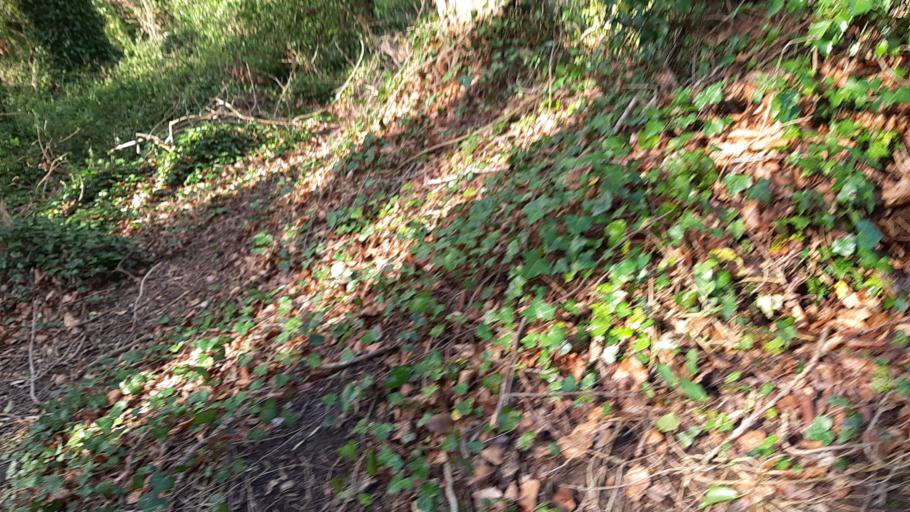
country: IE
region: Leinster
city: Malahide
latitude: 53.4417
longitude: -6.1715
